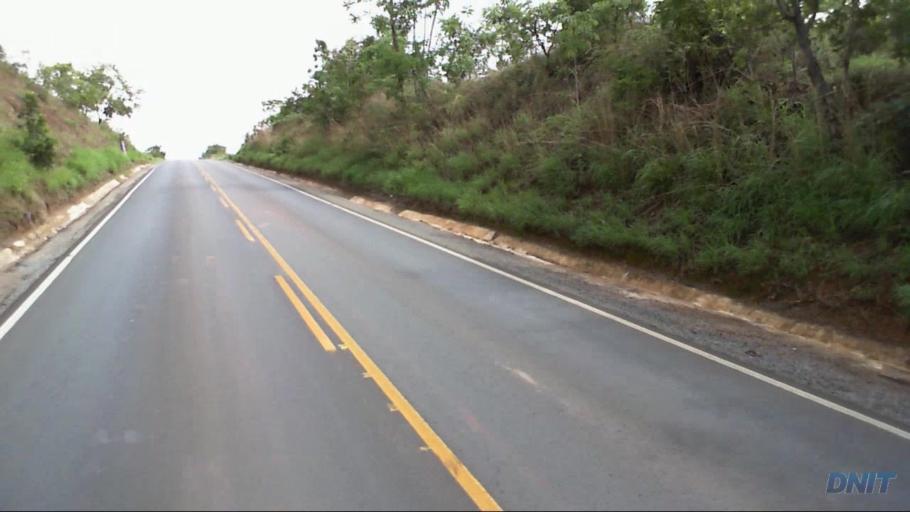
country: BR
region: Goias
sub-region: Padre Bernardo
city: Padre Bernardo
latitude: -15.2126
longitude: -48.2815
